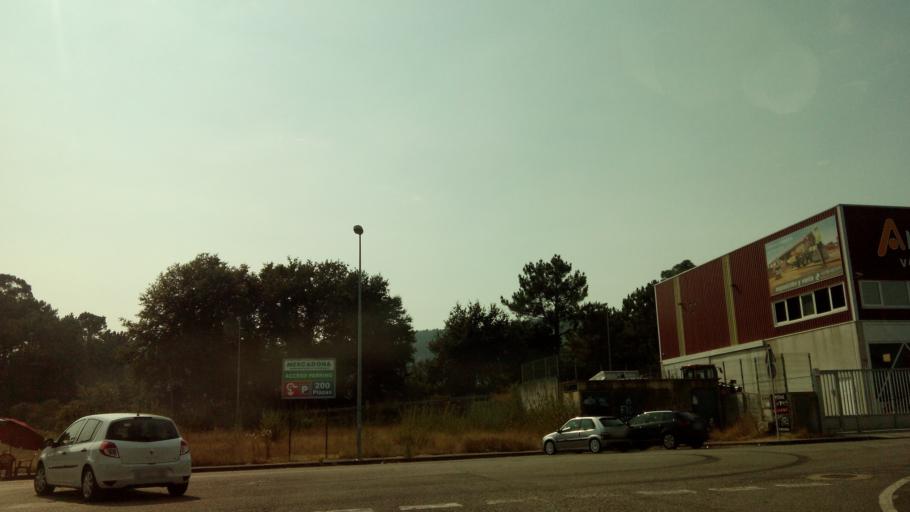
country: PT
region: Viana do Castelo
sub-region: Valenca
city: Valenca
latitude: 42.0378
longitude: -8.6657
